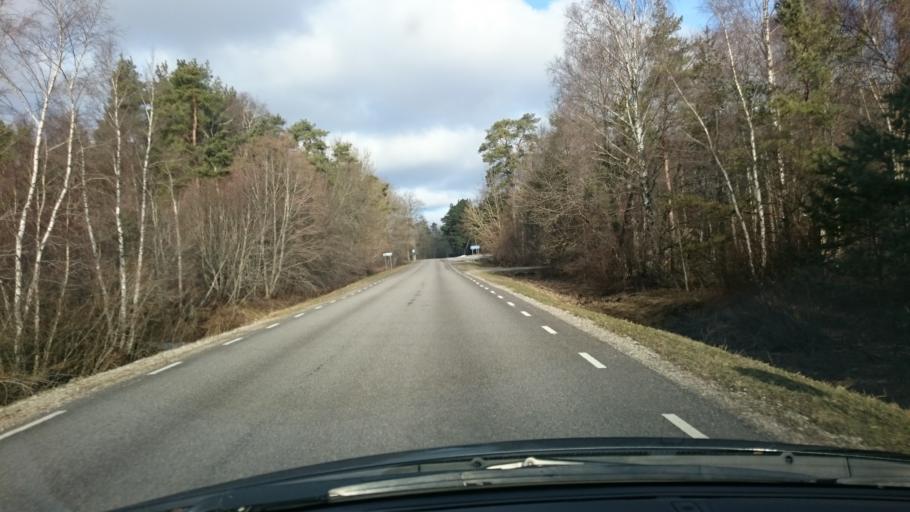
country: EE
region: Harju
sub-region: Keila linn
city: Keila
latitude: 59.3310
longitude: 24.3728
